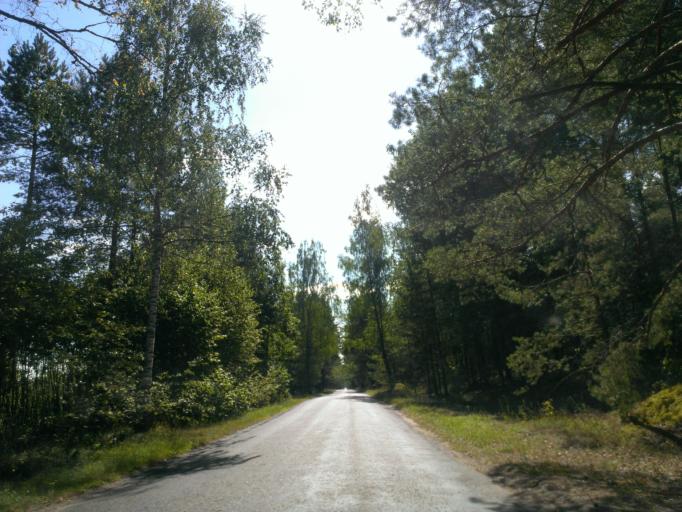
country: LV
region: Adazi
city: Adazi
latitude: 57.1117
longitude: 24.3457
